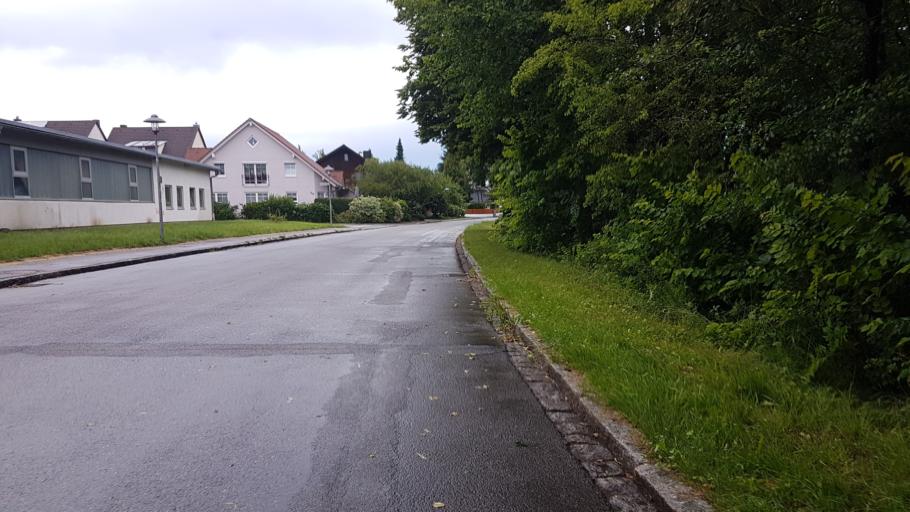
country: DE
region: Baden-Wuerttemberg
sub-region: Freiburg Region
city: Hufingen
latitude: 47.9374
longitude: 8.5017
